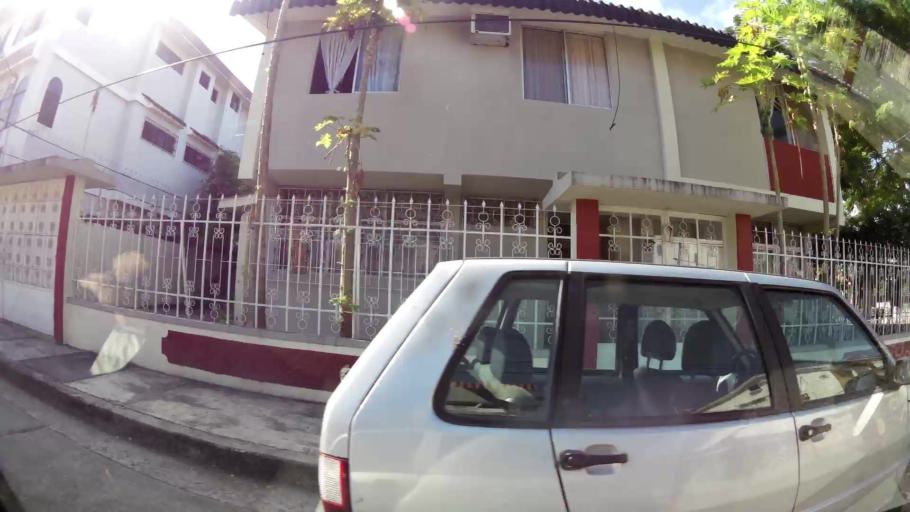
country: EC
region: Guayas
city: Guayaquil
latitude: -2.2269
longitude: -79.8926
